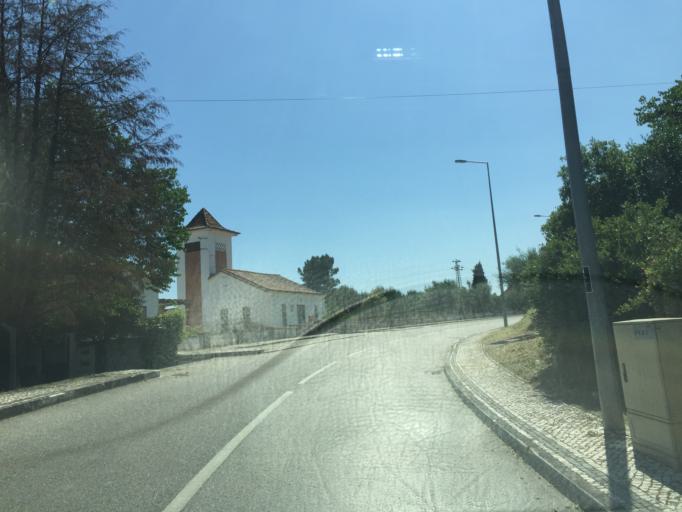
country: PT
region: Santarem
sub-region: Constancia
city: Constancia
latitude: 39.4811
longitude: -8.3315
